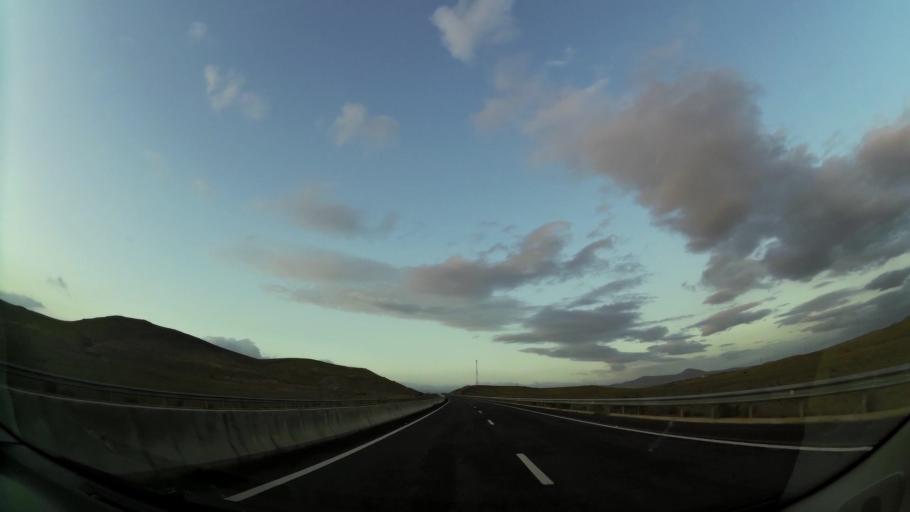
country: MA
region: Oriental
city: Taourirt
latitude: 34.5926
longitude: -2.7833
